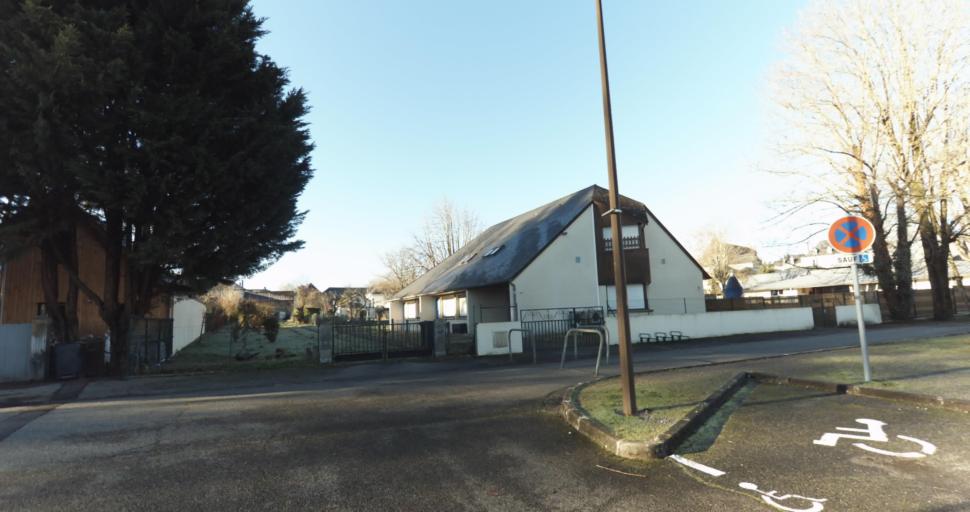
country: FR
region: Aquitaine
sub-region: Departement des Pyrenees-Atlantiques
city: Morlaas
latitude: 43.3444
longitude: -0.2604
